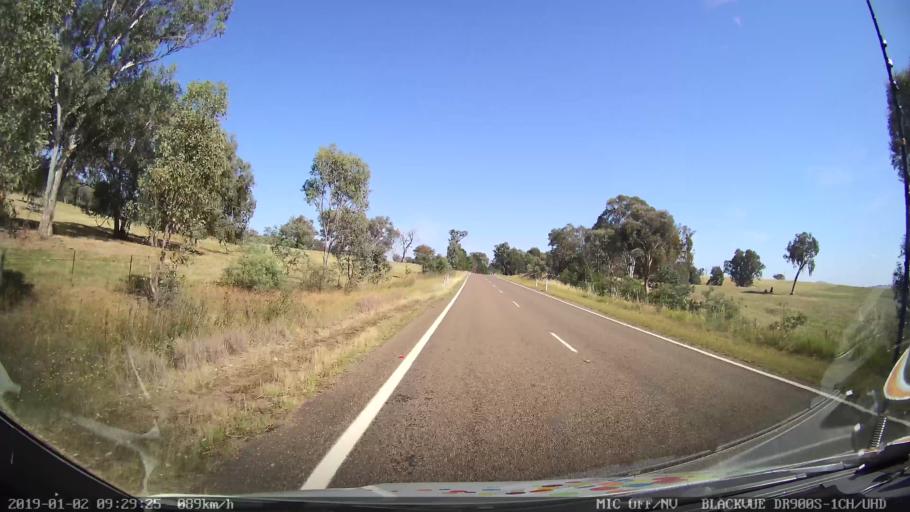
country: AU
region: New South Wales
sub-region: Tumut Shire
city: Tumut
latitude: -35.3388
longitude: 148.2426
